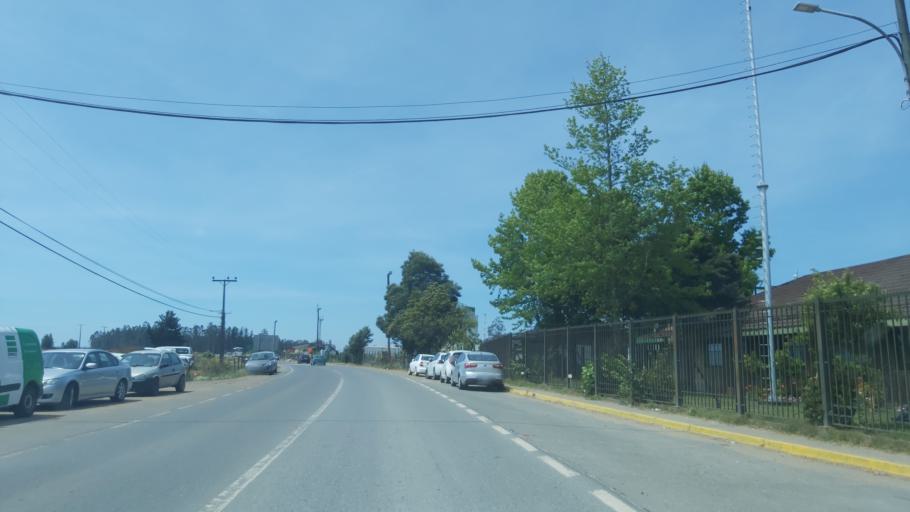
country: CL
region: Maule
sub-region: Provincia de Talca
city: Constitucion
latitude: -35.3737
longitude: -72.4151
